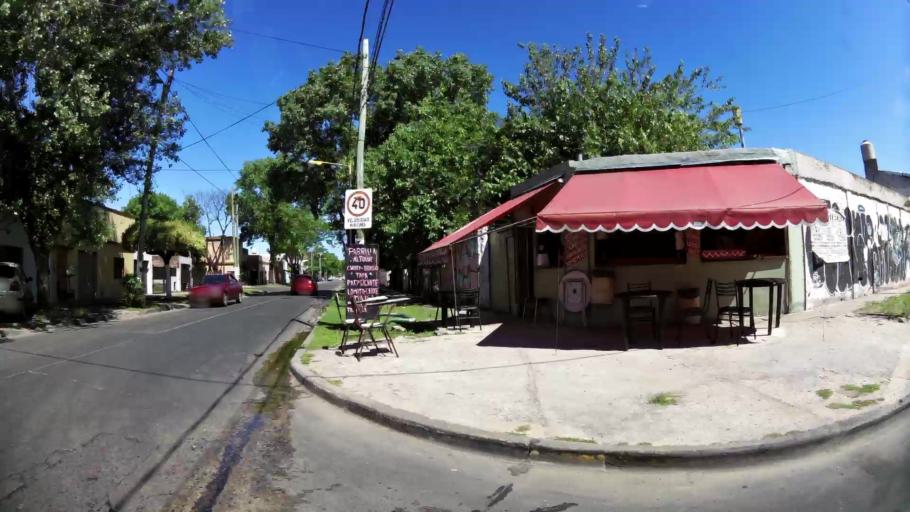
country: AR
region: Buenos Aires
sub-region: Partido de General San Martin
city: General San Martin
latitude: -34.5333
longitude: -58.5607
